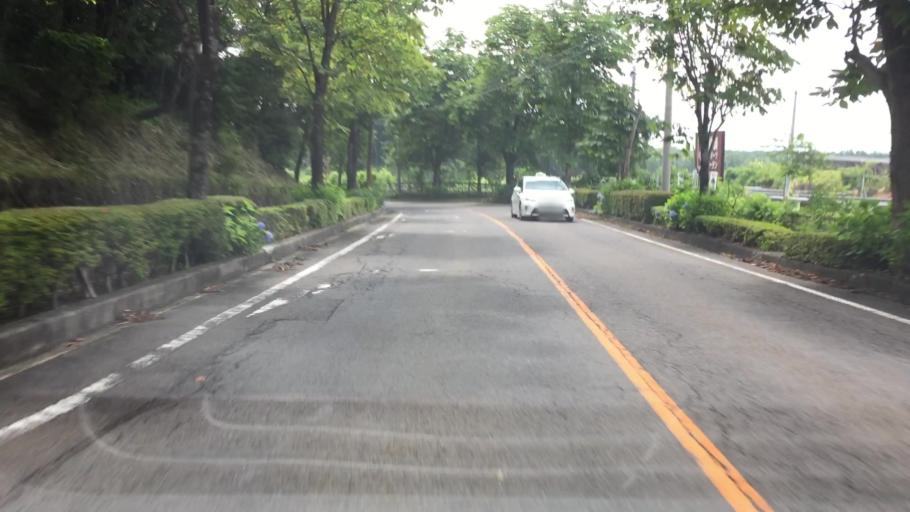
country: JP
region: Tochigi
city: Kuroiso
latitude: 37.0972
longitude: 140.0451
